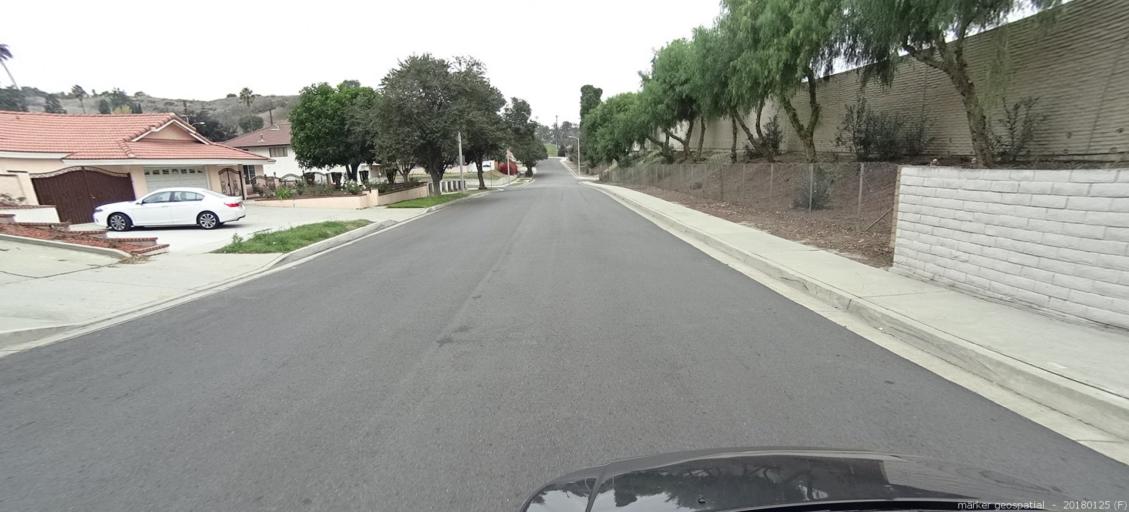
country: US
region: California
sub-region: Los Angeles County
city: Walnut
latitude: 33.9747
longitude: -117.8445
